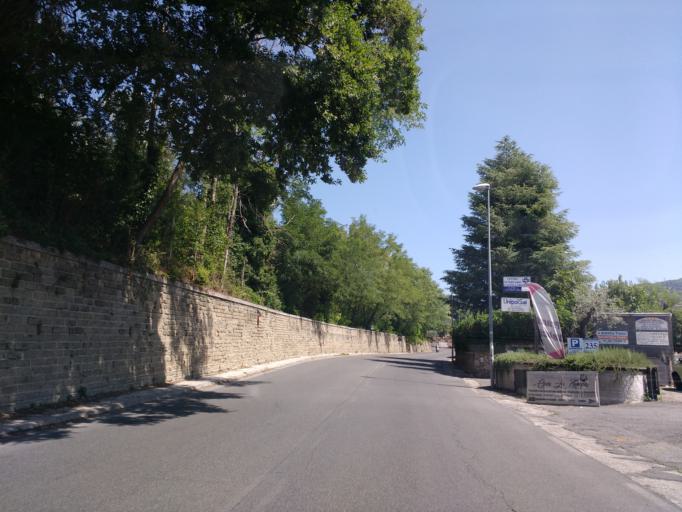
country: IT
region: Latium
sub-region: Citta metropolitana di Roma Capitale
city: Rocca di Papa
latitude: 41.7747
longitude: 12.6916
